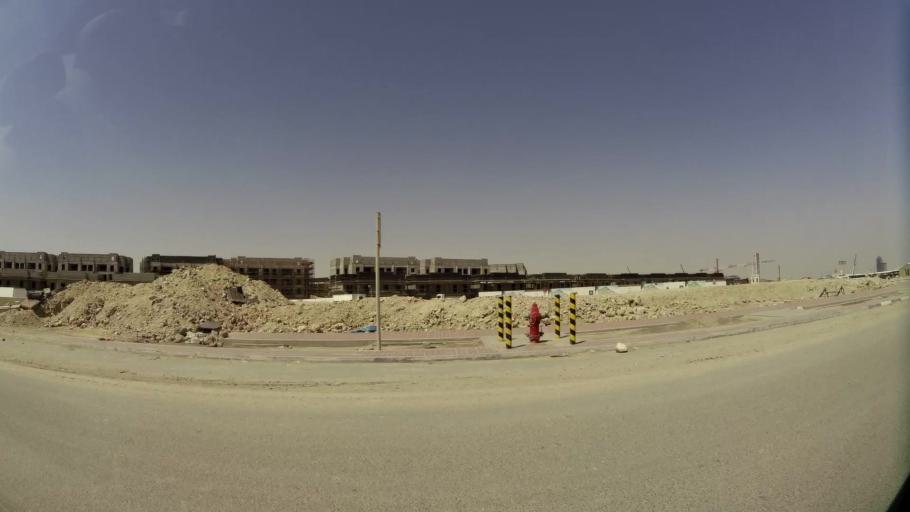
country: QA
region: Baladiyat Umm Salal
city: Umm Salal Muhammad
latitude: 25.4057
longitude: 51.5176
